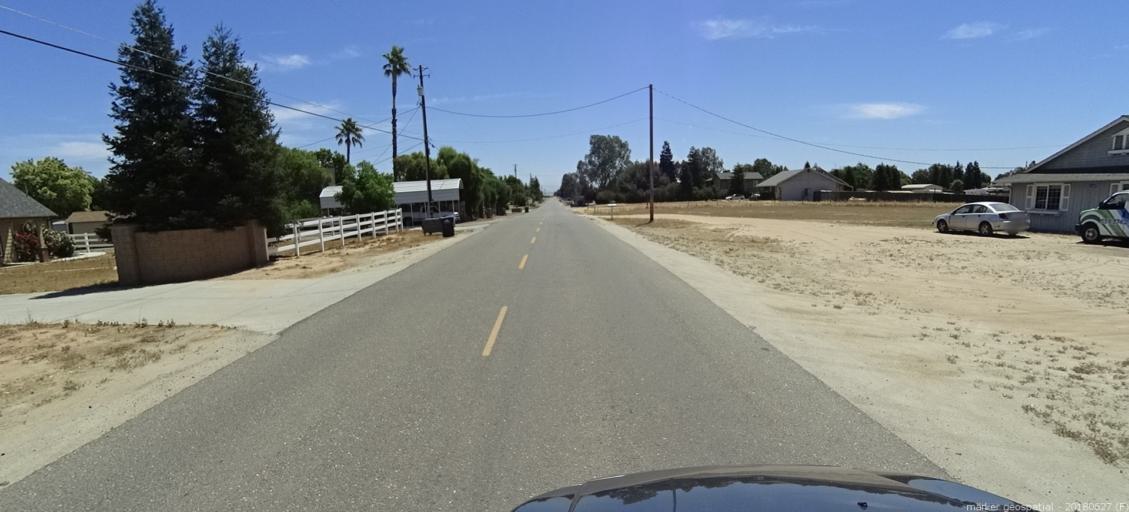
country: US
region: California
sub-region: Madera County
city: Bonadelle Ranchos-Madera Ranchos
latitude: 36.9375
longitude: -119.9026
